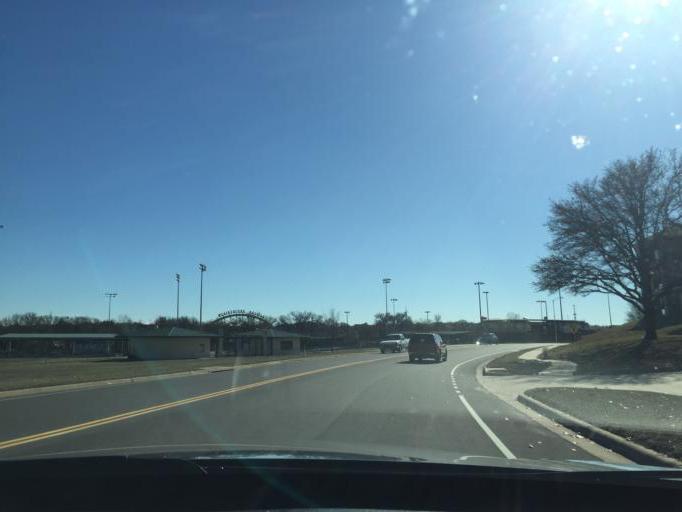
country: US
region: Texas
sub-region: Parker County
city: Weatherford
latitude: 32.7415
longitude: -97.7880
